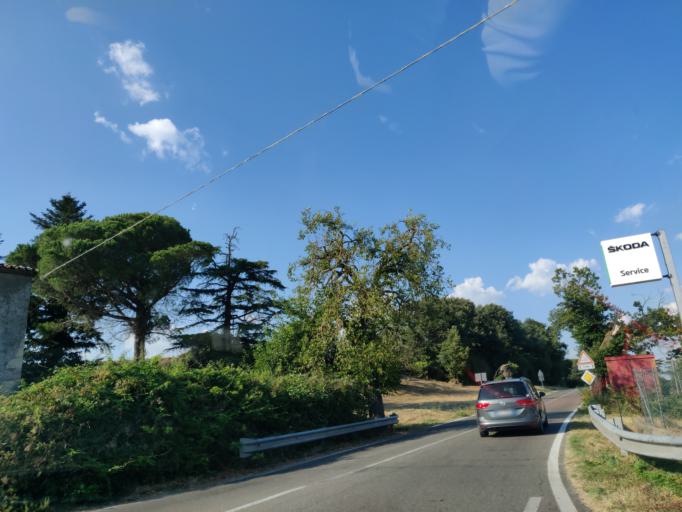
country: IT
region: Latium
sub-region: Provincia di Viterbo
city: Latera
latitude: 42.6327
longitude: 11.8343
